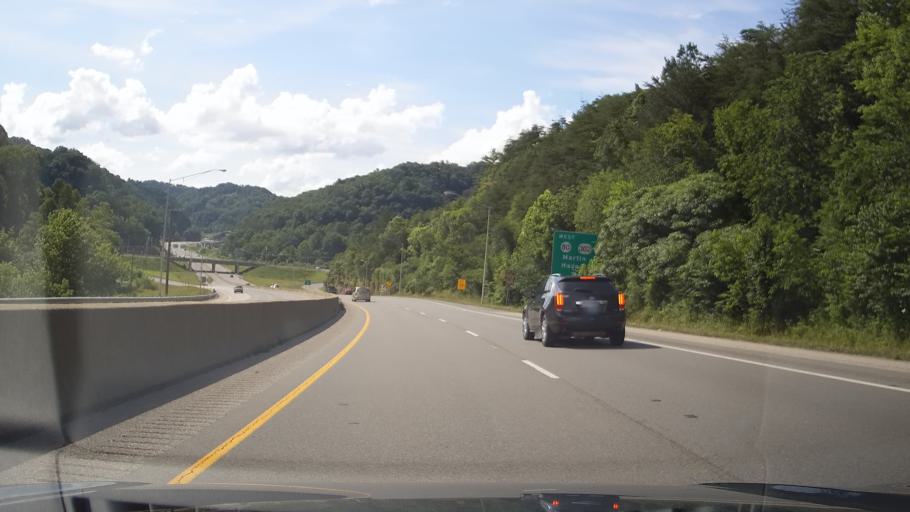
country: US
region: Kentucky
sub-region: Floyd County
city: Prestonsburg
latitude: 37.6335
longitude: -82.7429
